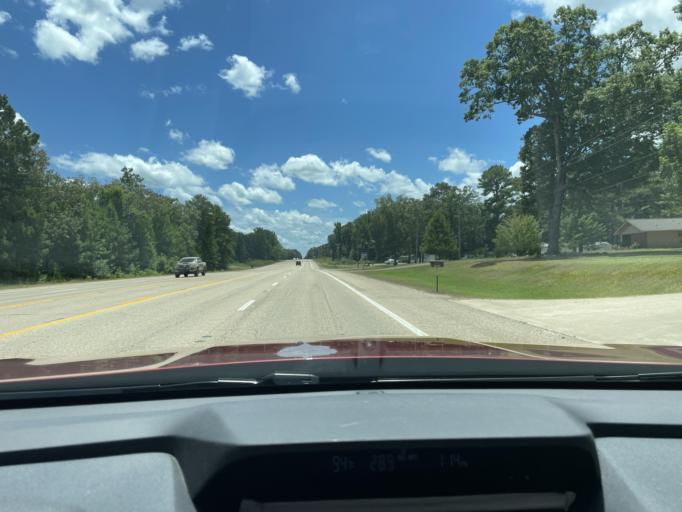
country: US
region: Arkansas
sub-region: Drew County
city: Monticello
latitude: 33.6658
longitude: -91.8038
